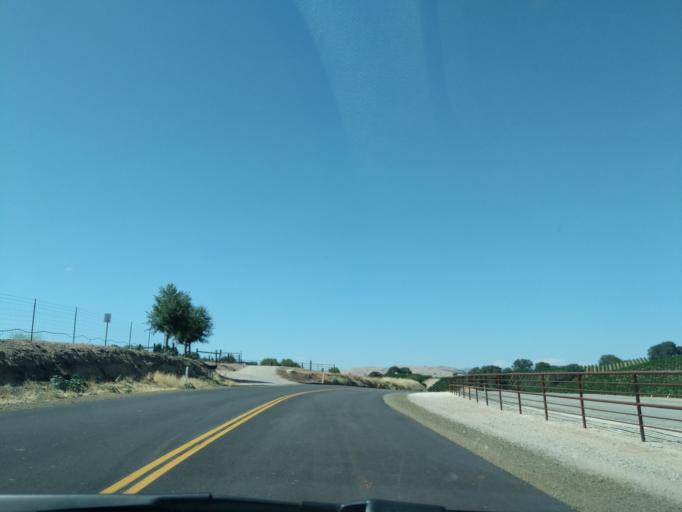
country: US
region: California
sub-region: San Luis Obispo County
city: San Miguel
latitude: 35.7025
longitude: -120.6405
